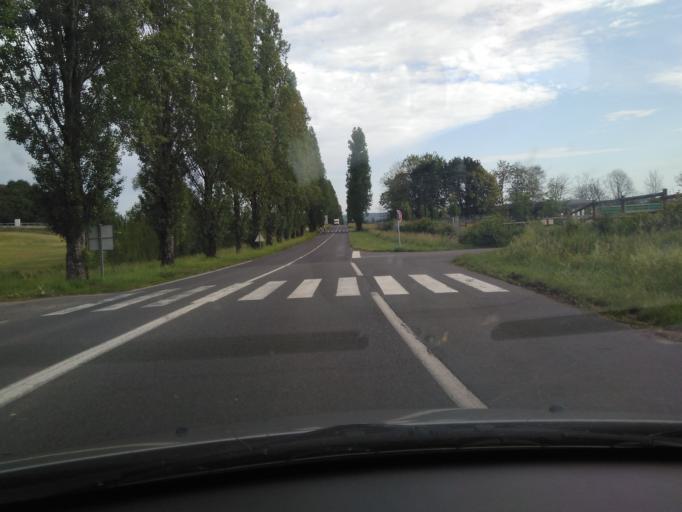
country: FR
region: Centre
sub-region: Departement d'Indre-et-Loire
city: Amboise
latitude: 47.3928
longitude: 0.9795
